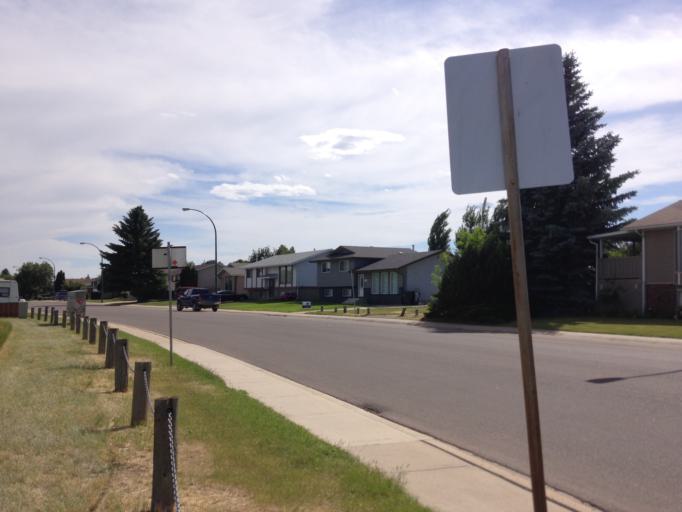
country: CA
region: Alberta
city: Medicine Hat
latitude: 50.0043
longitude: -110.6251
